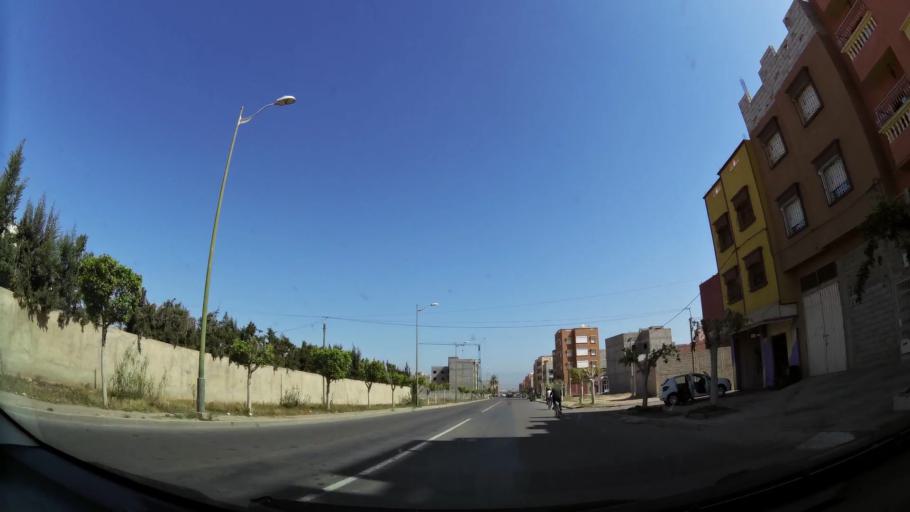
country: MA
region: Souss-Massa-Draa
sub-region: Inezgane-Ait Mellou
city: Inezgane
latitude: 30.3425
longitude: -9.5081
